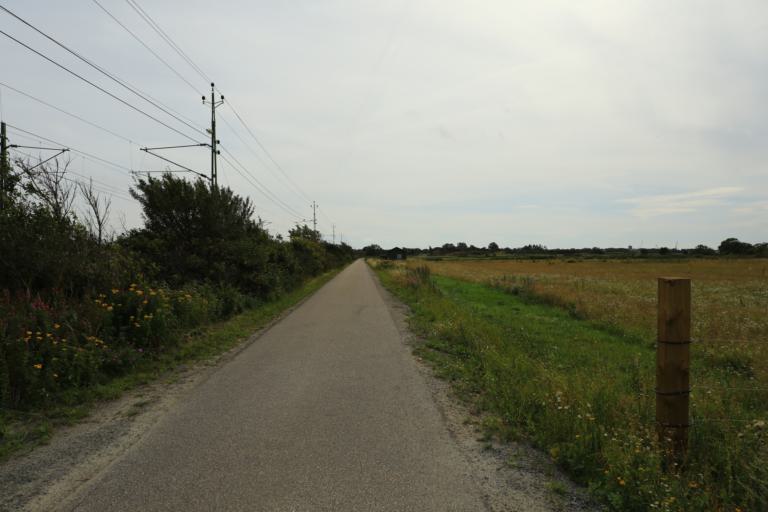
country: SE
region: Halland
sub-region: Varbergs Kommun
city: Varberg
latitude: 57.1362
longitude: 12.2596
